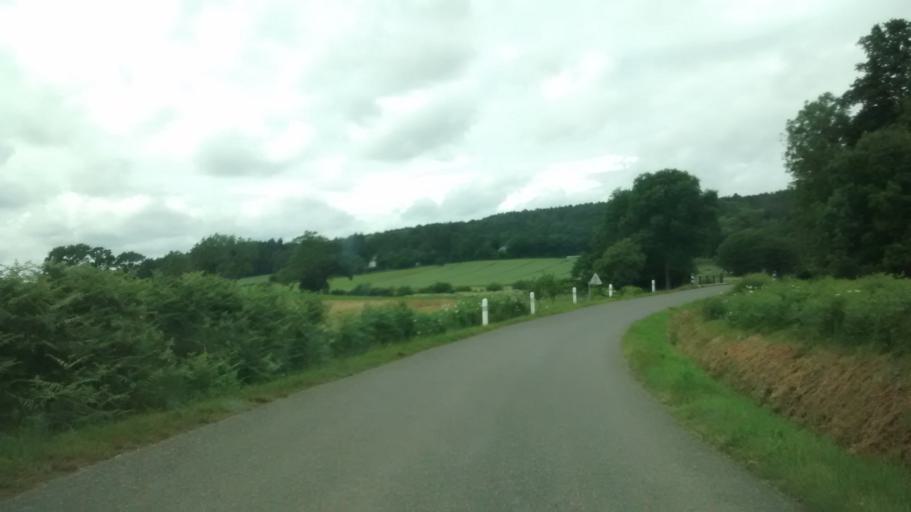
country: FR
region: Brittany
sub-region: Departement du Morbihan
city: Carentoir
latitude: 47.8385
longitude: -2.2073
